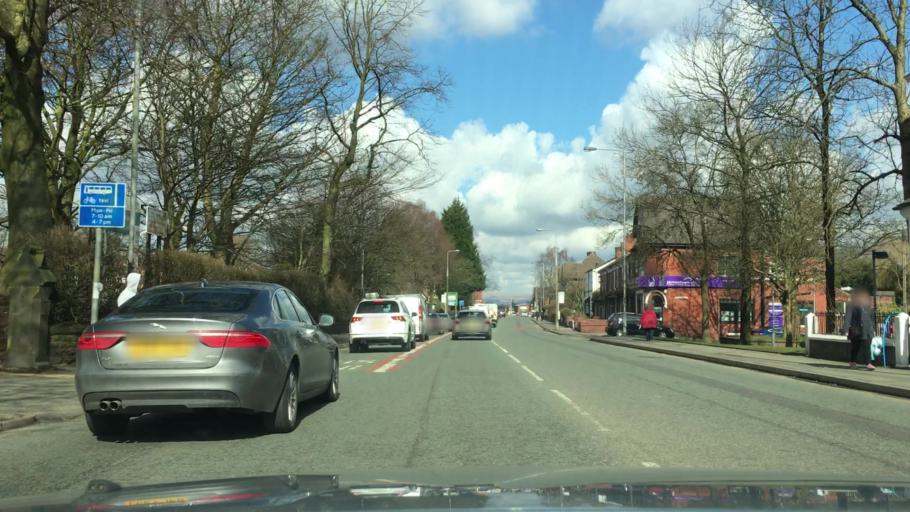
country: GB
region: England
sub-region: Borough of Bury
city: Whitefield
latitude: 53.5491
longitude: -2.2946
